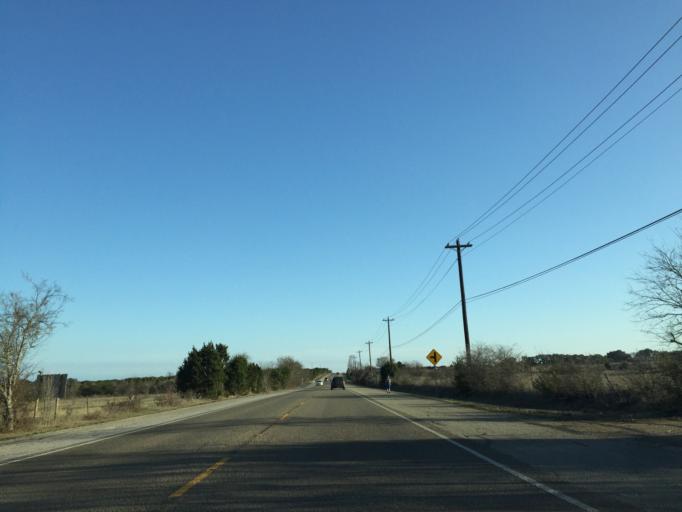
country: US
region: Texas
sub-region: Williamson County
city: Florence
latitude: 30.7530
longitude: -97.8072
